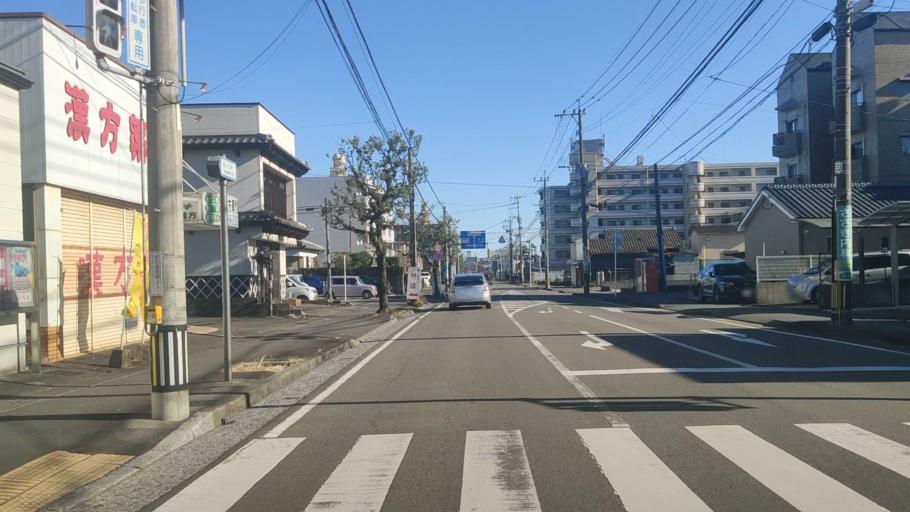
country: JP
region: Miyazaki
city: Miyazaki-shi
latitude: 31.8964
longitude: 131.4299
